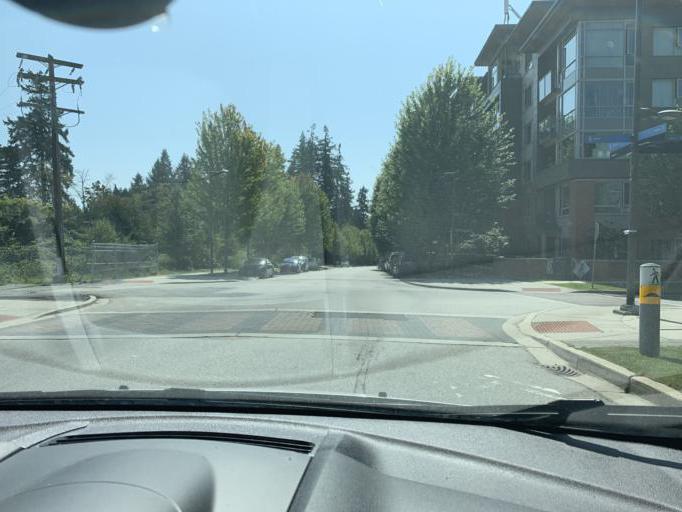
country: CA
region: British Columbia
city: West End
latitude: 49.2515
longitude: -123.2332
